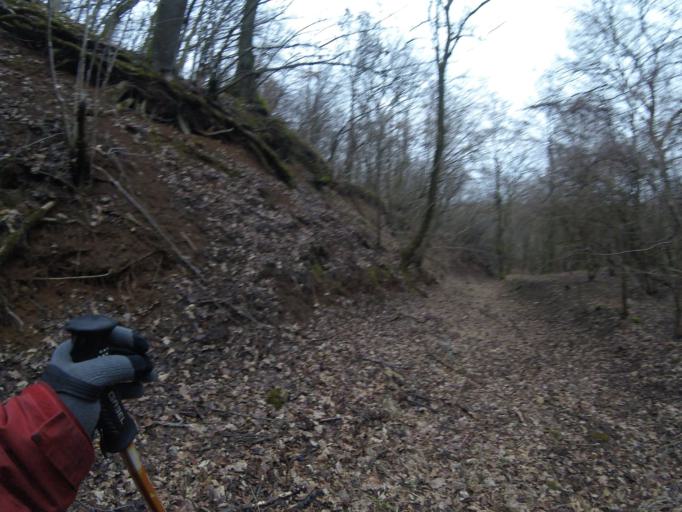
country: HU
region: Borsod-Abauj-Zemplen
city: Rudabanya
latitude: 48.4479
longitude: 20.6073
